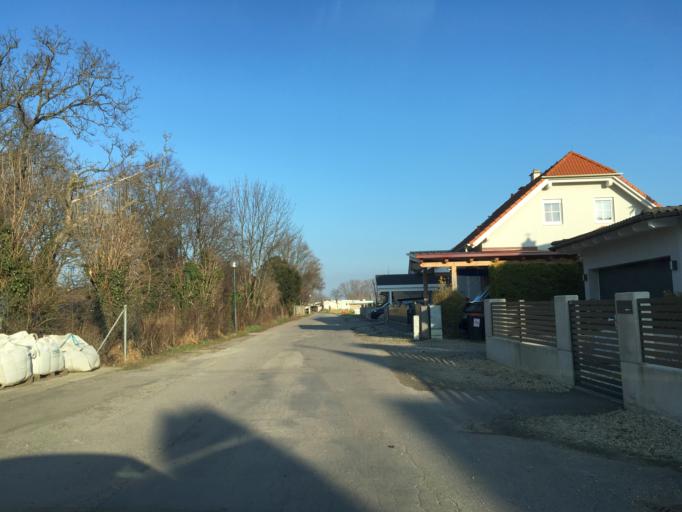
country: AT
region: Lower Austria
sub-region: Politischer Bezirk Tulln
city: Konigstetten
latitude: 48.3315
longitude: 16.1257
